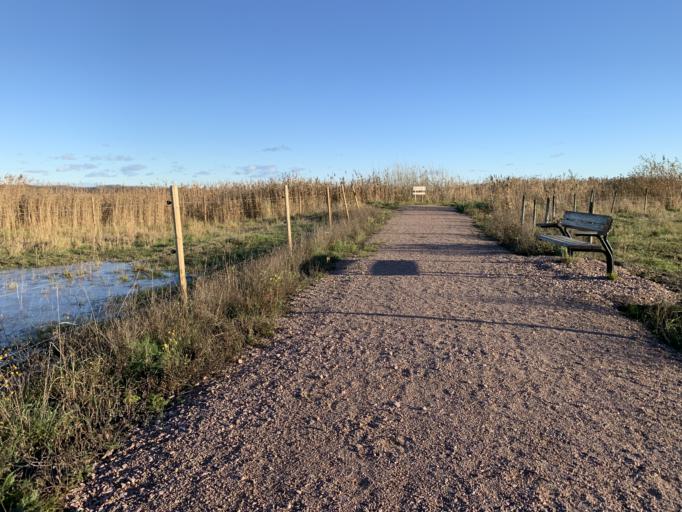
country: SE
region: Soedermanland
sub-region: Eskilstuna Kommun
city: Torshalla
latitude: 59.5228
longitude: 16.4503
